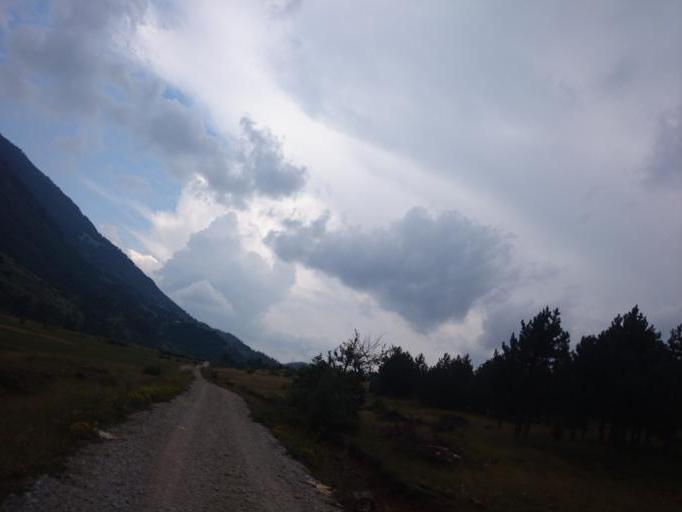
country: AL
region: Diber
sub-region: Rrethi i Dibres
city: Fushe-Lure
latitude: 41.7967
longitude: 20.2263
